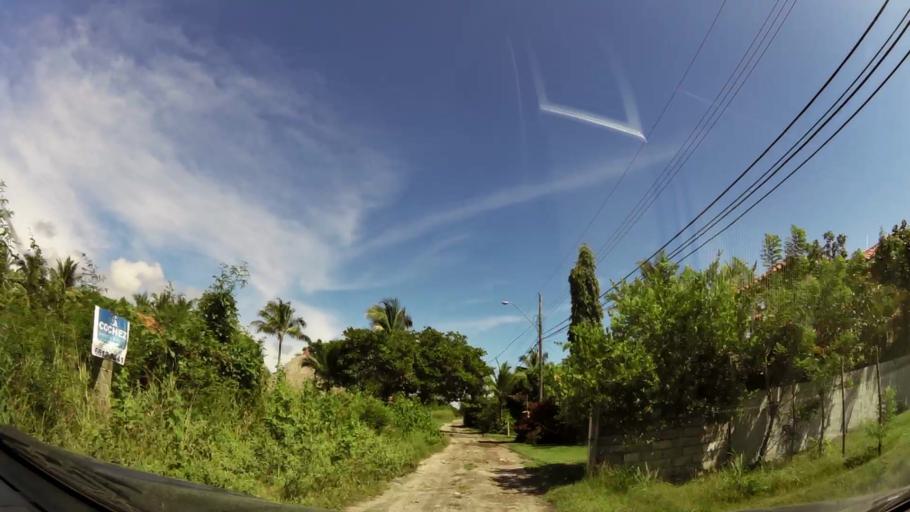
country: PA
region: Panama
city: Nueva Gorgona
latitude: 8.5562
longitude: -79.8551
